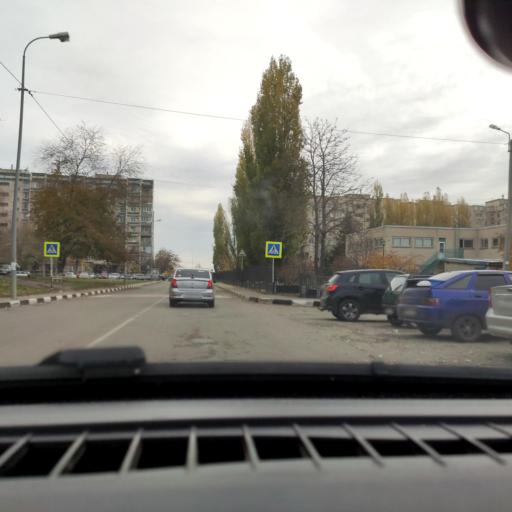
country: RU
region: Belgorod
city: Alekseyevka
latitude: 50.6271
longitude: 38.6984
